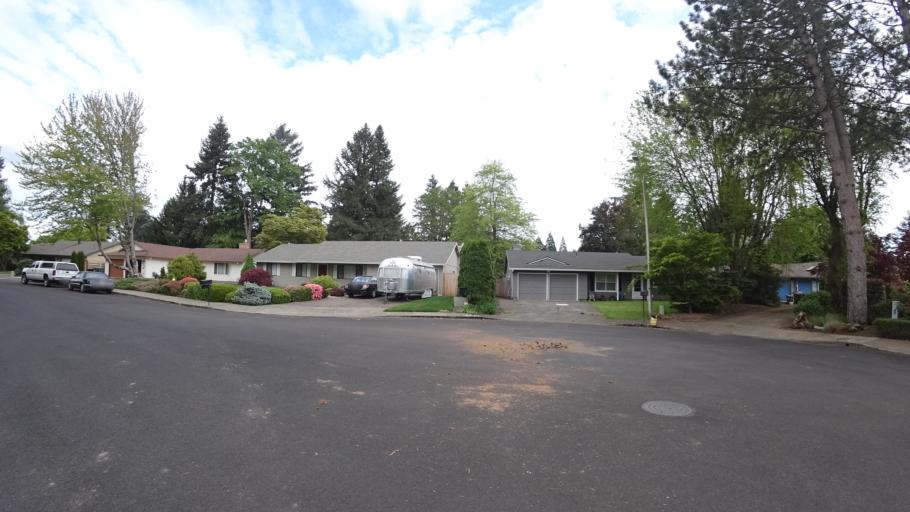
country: US
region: Oregon
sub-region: Washington County
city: Hillsboro
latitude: 45.4927
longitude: -122.9617
